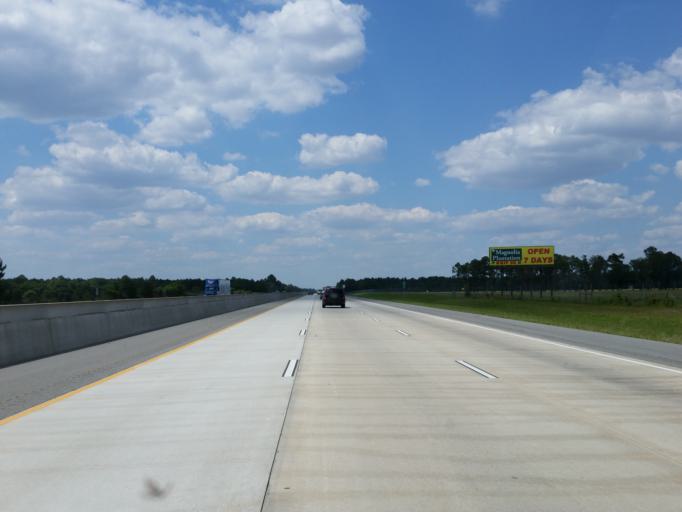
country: US
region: Georgia
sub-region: Cook County
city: Sparks
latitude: 31.1895
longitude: -83.4547
